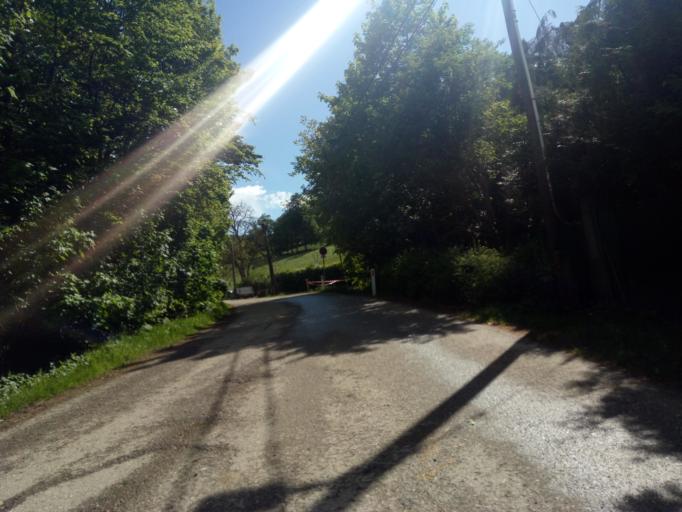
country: AT
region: Lower Austria
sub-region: Politischer Bezirk Modling
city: Breitenfurt bei Wien
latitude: 48.1304
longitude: 16.1463
